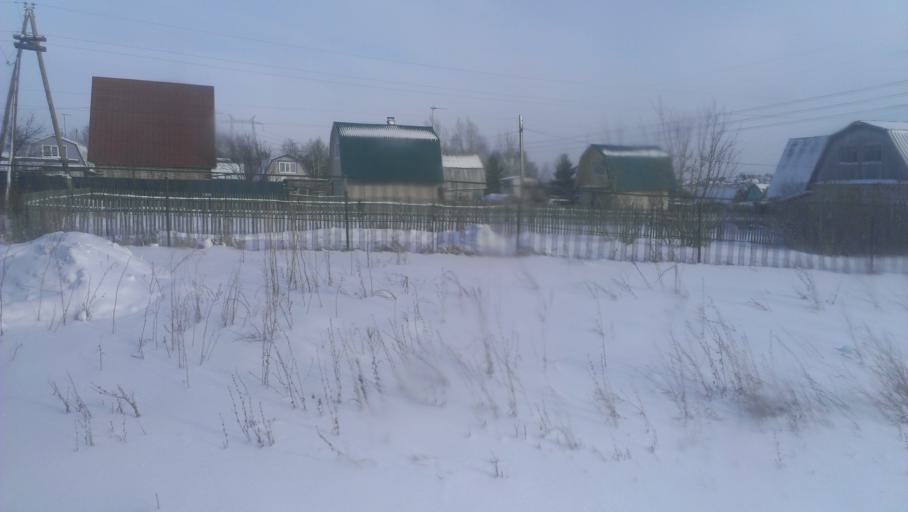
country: RU
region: Altai Krai
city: Gon'ba
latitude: 53.4171
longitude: 83.5495
